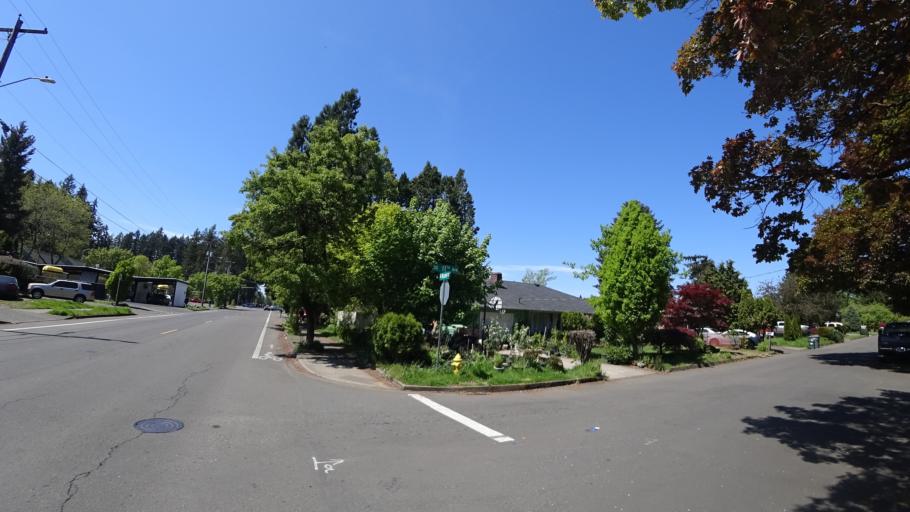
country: US
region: Oregon
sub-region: Washington County
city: Hillsboro
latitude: 45.5149
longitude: -122.9722
